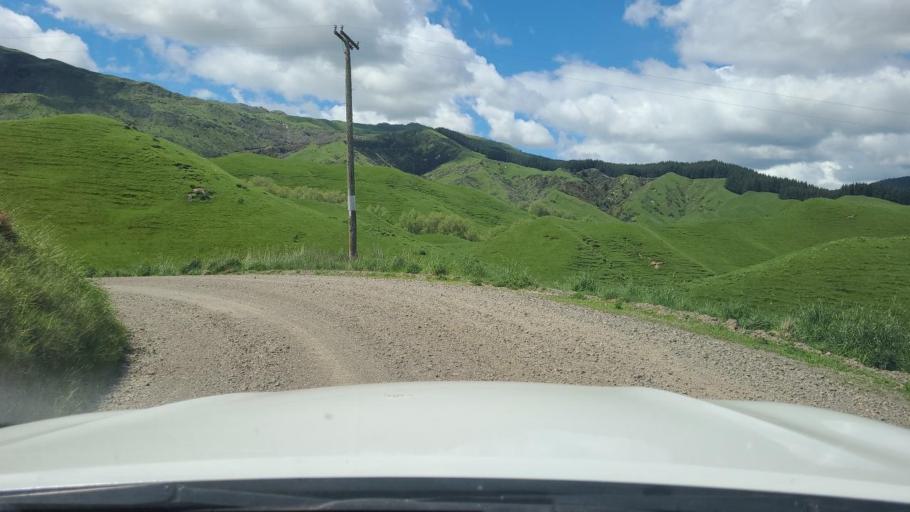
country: NZ
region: Hawke's Bay
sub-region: Napier City
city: Napier
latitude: -39.1646
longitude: 176.6723
